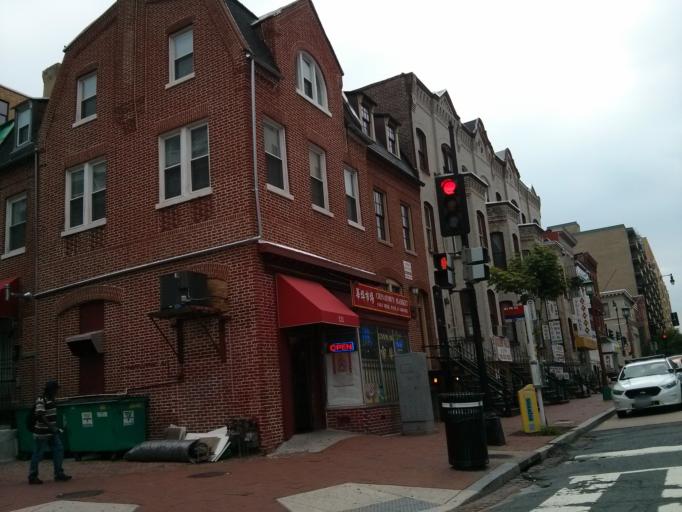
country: US
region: Washington, D.C.
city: Washington, D.C.
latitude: 38.8998
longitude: -77.0198
